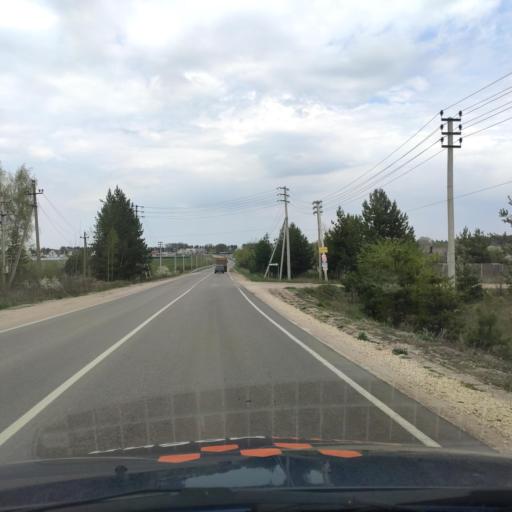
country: RU
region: Voronezj
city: Podgornoye
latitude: 51.8665
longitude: 39.1710
